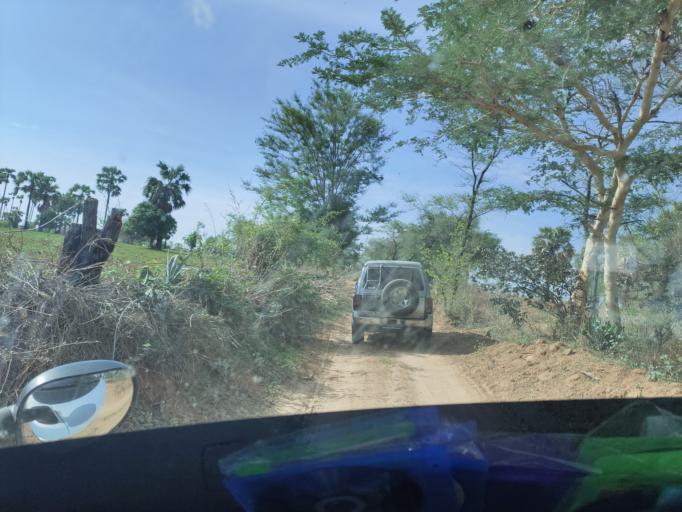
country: MM
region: Magway
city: Chauk
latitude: 20.9550
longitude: 94.9925
